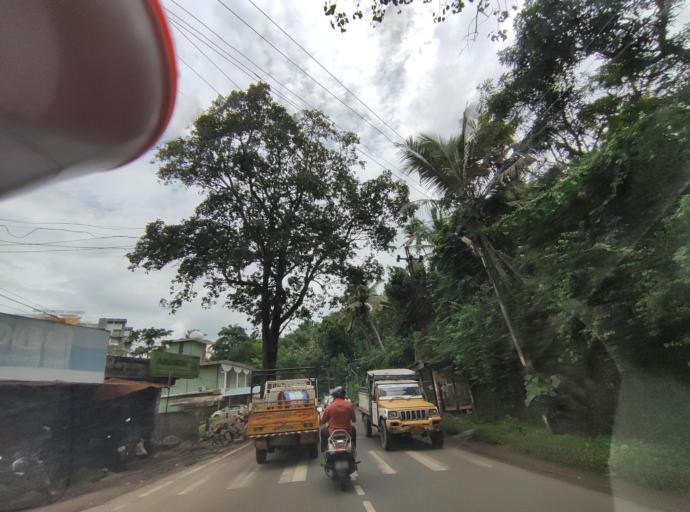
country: IN
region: Kerala
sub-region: Thiruvananthapuram
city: Nedumangad
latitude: 8.5847
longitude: 76.9493
